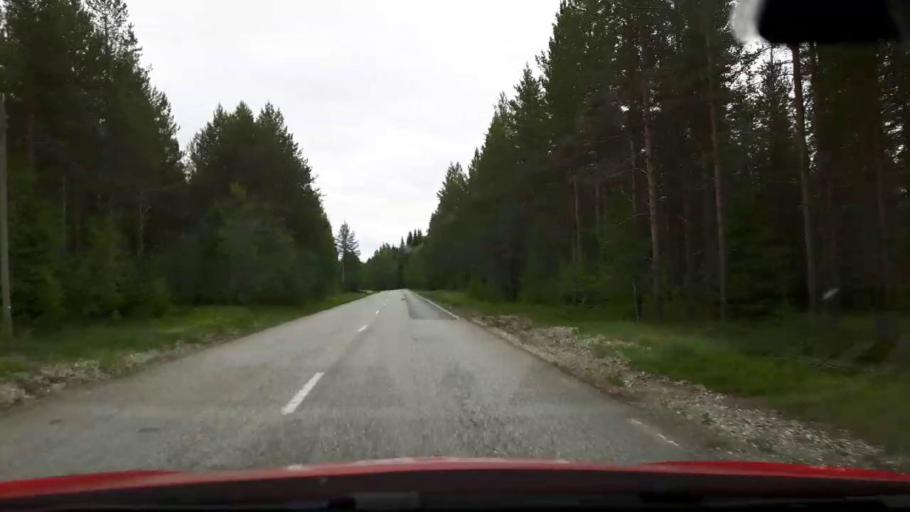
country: SE
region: Jaemtland
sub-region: Ragunda Kommun
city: Hammarstrand
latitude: 63.2385
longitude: 15.9166
